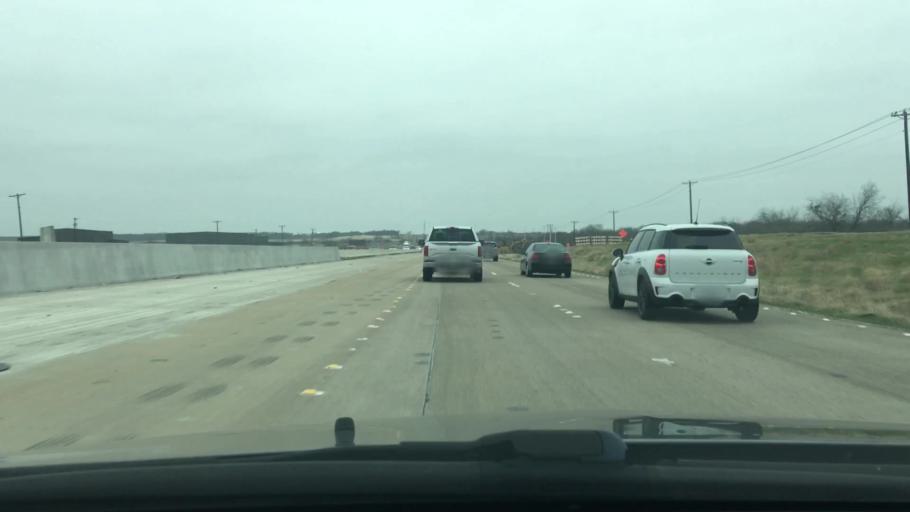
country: US
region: Texas
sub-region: Navarro County
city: Corsicana
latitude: 32.0549
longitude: -96.4507
